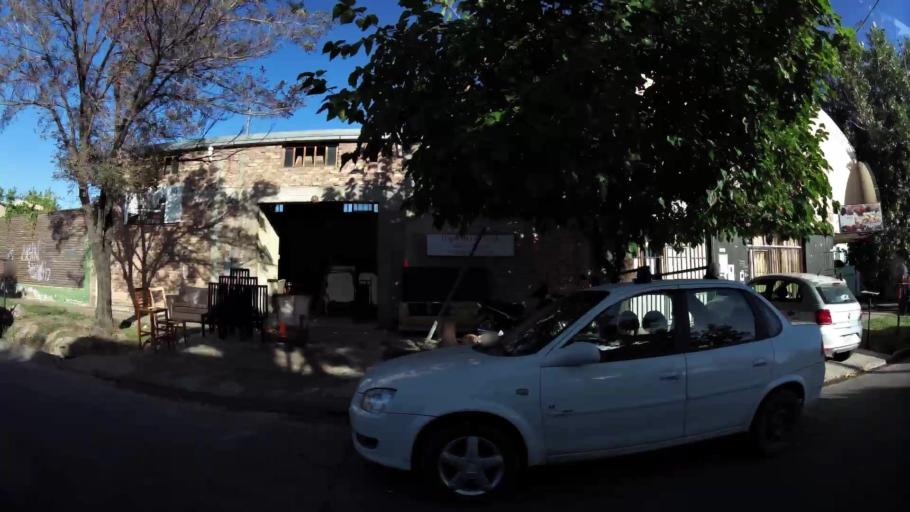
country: AR
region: Mendoza
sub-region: Departamento de Godoy Cruz
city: Godoy Cruz
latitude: -32.9267
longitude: -68.8406
